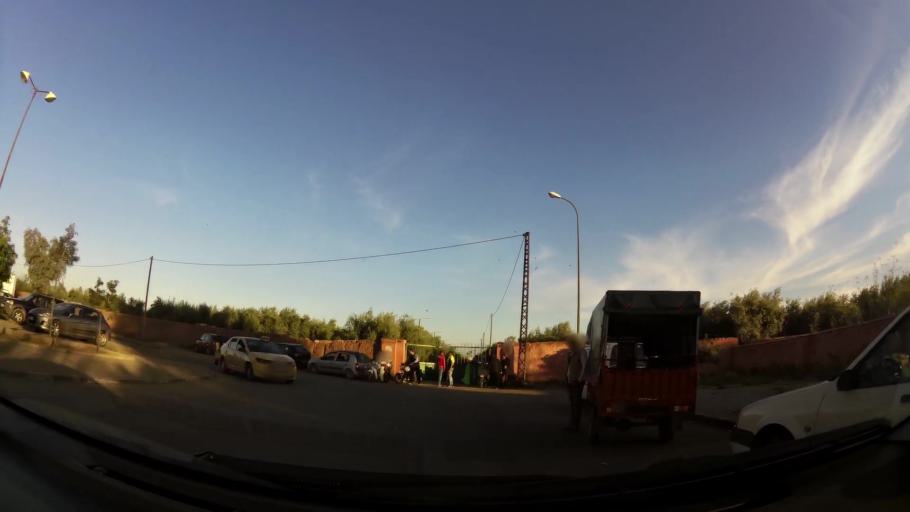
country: MA
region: Marrakech-Tensift-Al Haouz
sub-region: Marrakech
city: Marrakesh
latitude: 31.6190
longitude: -8.0259
